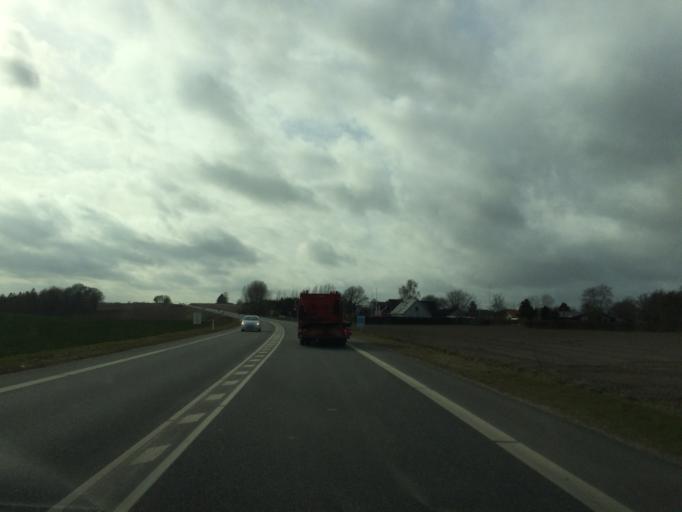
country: DK
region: Central Jutland
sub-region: Randers Kommune
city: Langa
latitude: 56.4794
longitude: 9.8982
